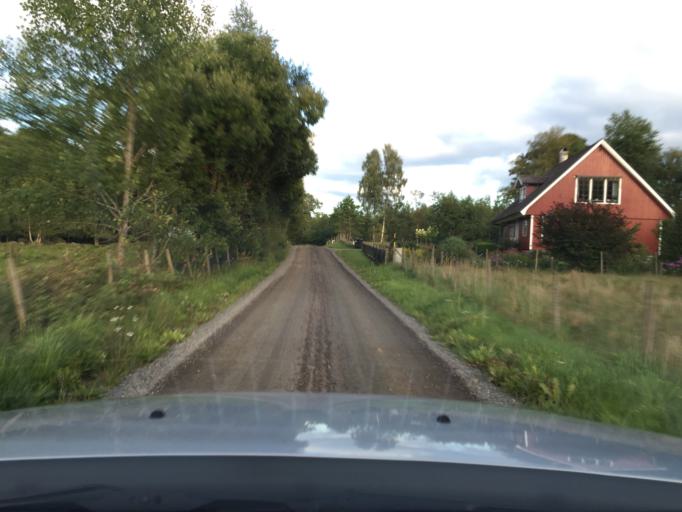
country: SE
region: Skane
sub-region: Hassleholms Kommun
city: Sosdala
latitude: 56.0371
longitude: 13.7104
